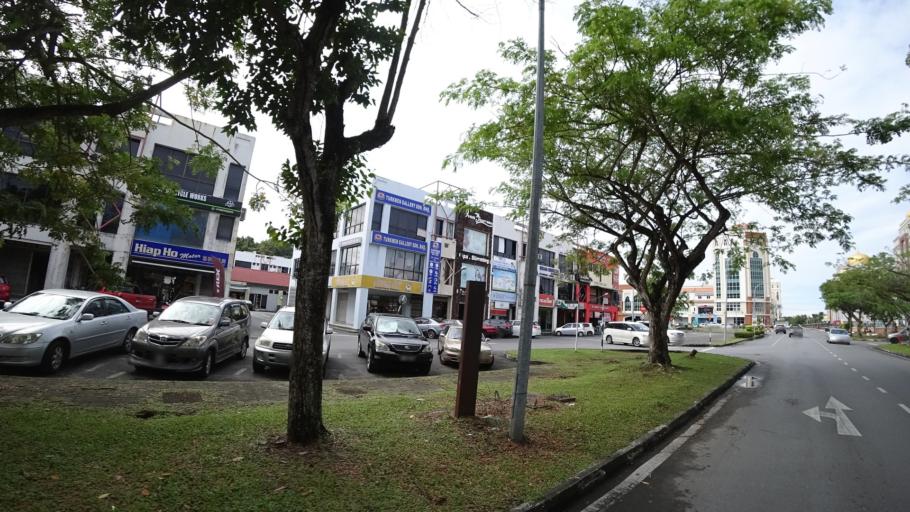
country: MY
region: Sarawak
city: Miri
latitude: 4.4149
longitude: 114.0116
